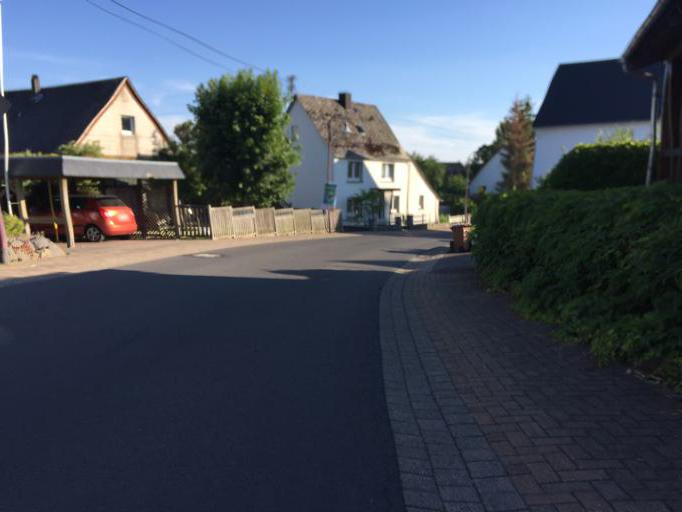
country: DE
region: Rheinland-Pfalz
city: Hartlingen
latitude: 50.5297
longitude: 7.9122
